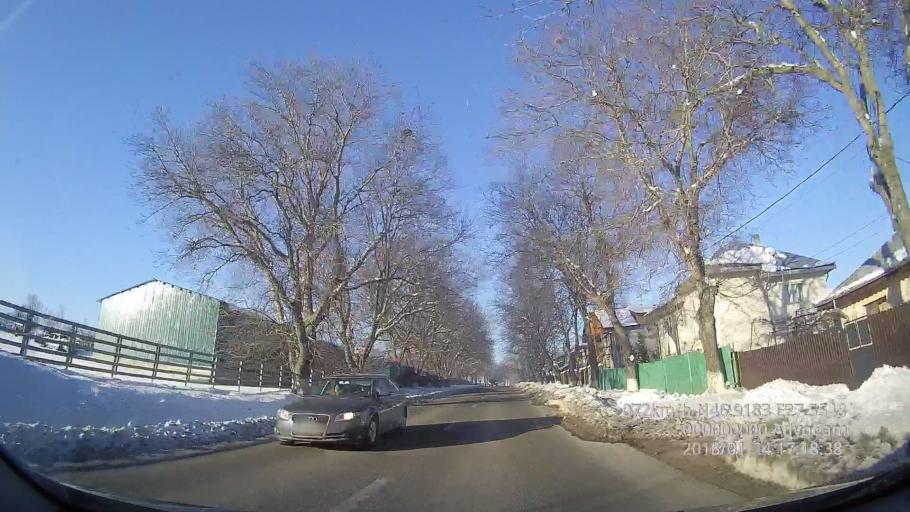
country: RO
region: Iasi
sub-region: Comuna Scanteia
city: Scanteia
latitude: 46.9189
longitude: 27.5647
